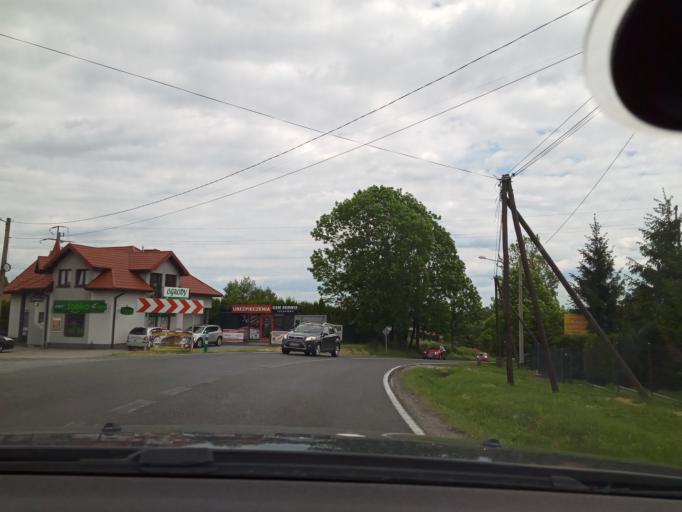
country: PL
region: Lesser Poland Voivodeship
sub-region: Powiat wielicki
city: Trabki
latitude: 49.9722
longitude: 20.1273
